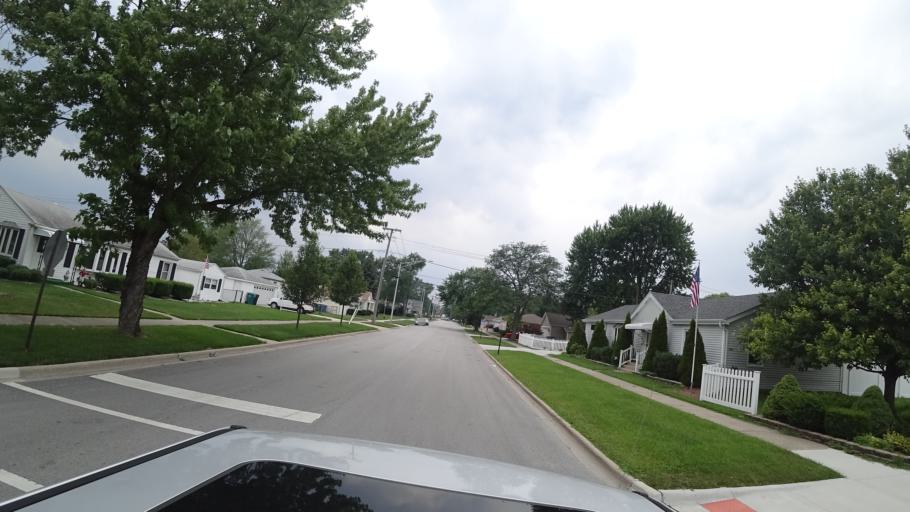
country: US
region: Illinois
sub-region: Cook County
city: Chicago Ridge
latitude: 41.6923
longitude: -87.7753
